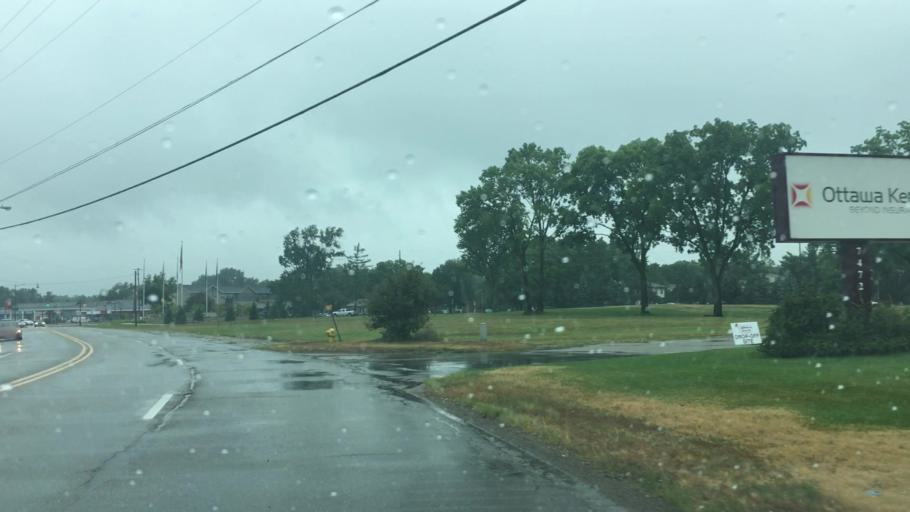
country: US
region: Michigan
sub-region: Ottawa County
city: Jenison
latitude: 42.9056
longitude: -85.7862
